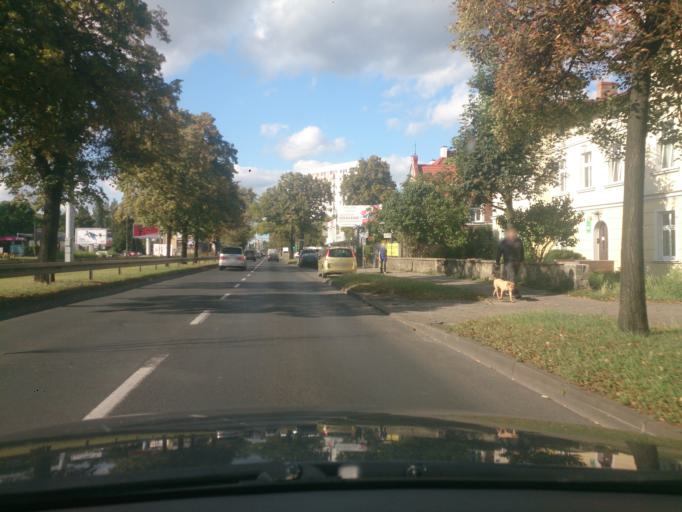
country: PL
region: Pomeranian Voivodeship
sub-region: Sopot
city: Sopot
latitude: 54.4167
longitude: 18.5659
